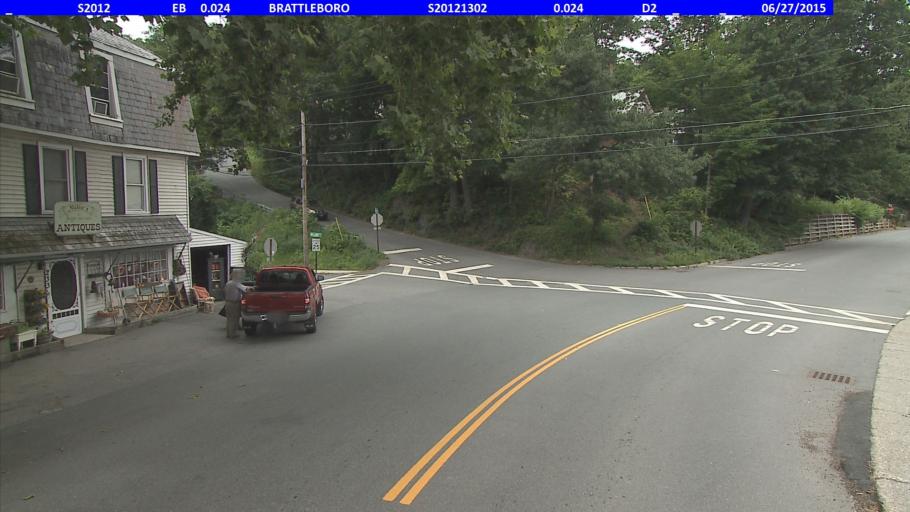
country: US
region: Vermont
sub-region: Windham County
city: Brattleboro
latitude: 42.8498
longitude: -72.5677
